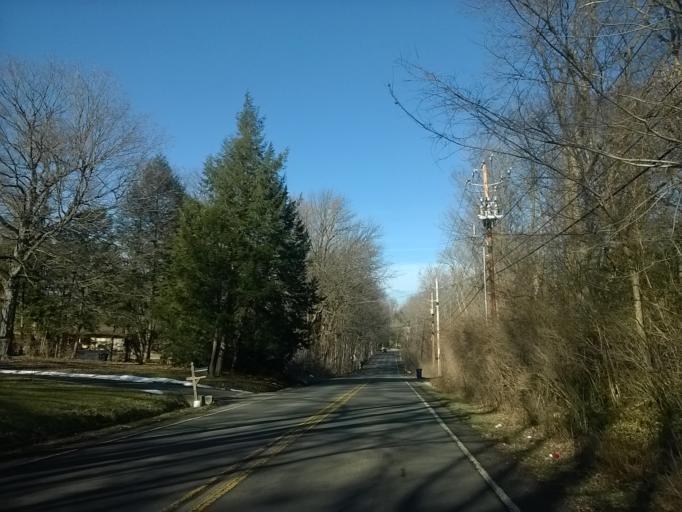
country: US
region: Indiana
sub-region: Marion County
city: Meridian Hills
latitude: 39.8982
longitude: -86.1650
